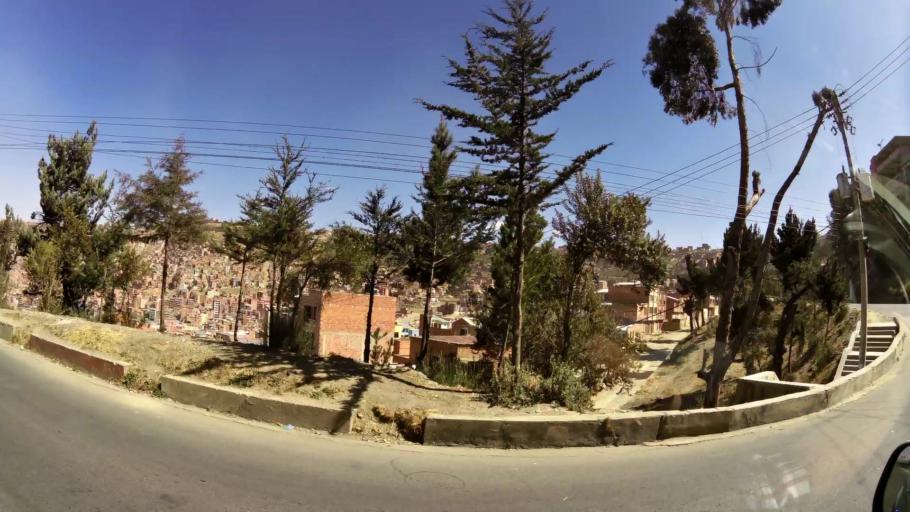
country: BO
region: La Paz
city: La Paz
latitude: -16.4867
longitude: -68.1617
